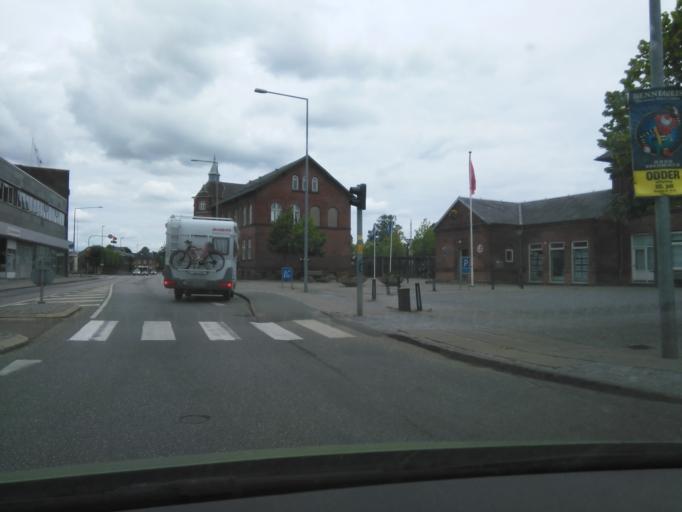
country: DK
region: Central Jutland
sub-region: Odder Kommune
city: Odder
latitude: 55.9719
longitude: 10.1496
